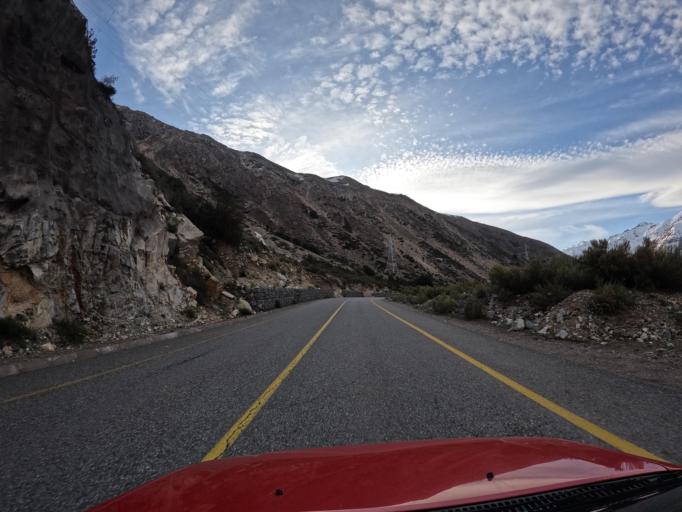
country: CL
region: Maule
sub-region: Provincia de Linares
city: Colbun
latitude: -35.8731
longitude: -70.6798
